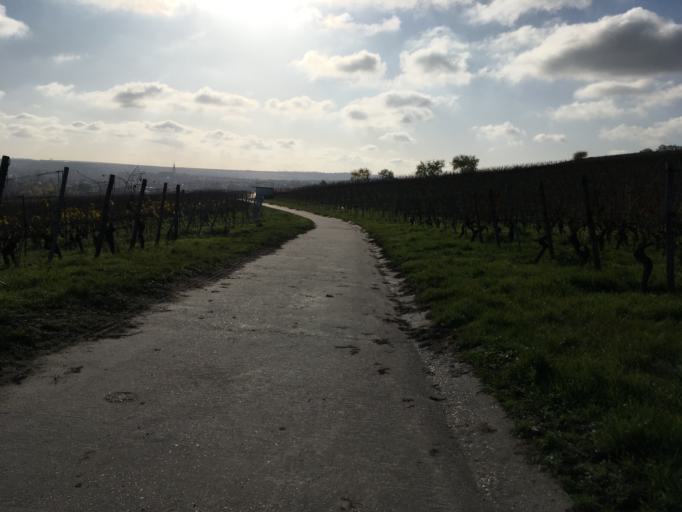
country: DE
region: Rheinland-Pfalz
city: Bodenheim
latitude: 49.9442
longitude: 8.3020
